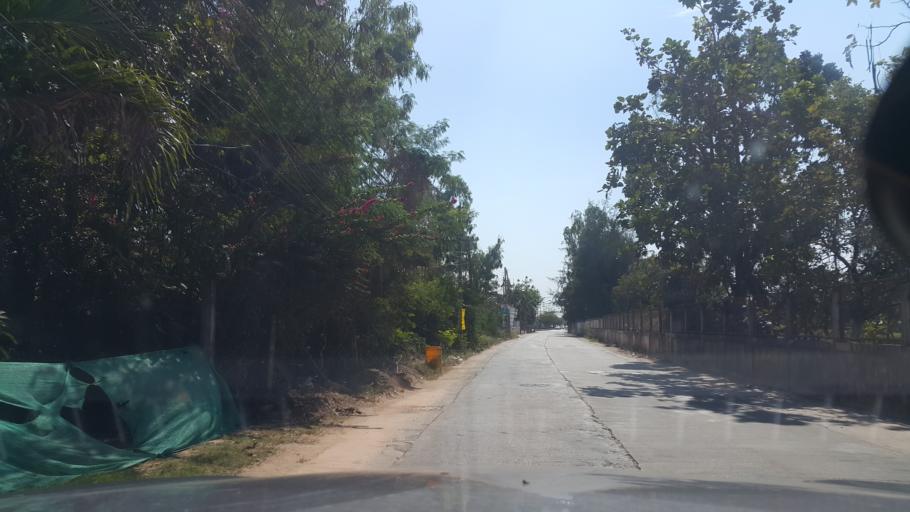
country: TH
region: Changwat Udon Thani
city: Udon Thani
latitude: 17.4515
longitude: 102.7832
